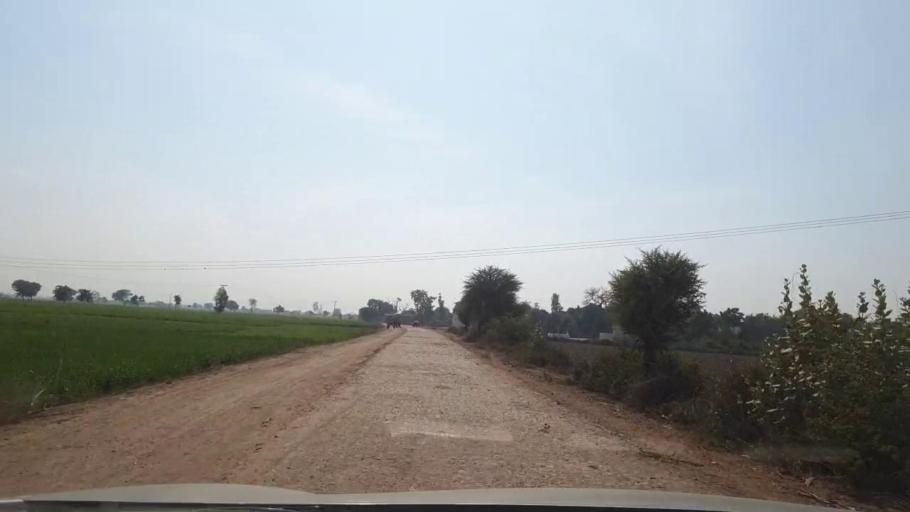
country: PK
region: Sindh
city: Berani
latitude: 25.6295
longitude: 68.7623
